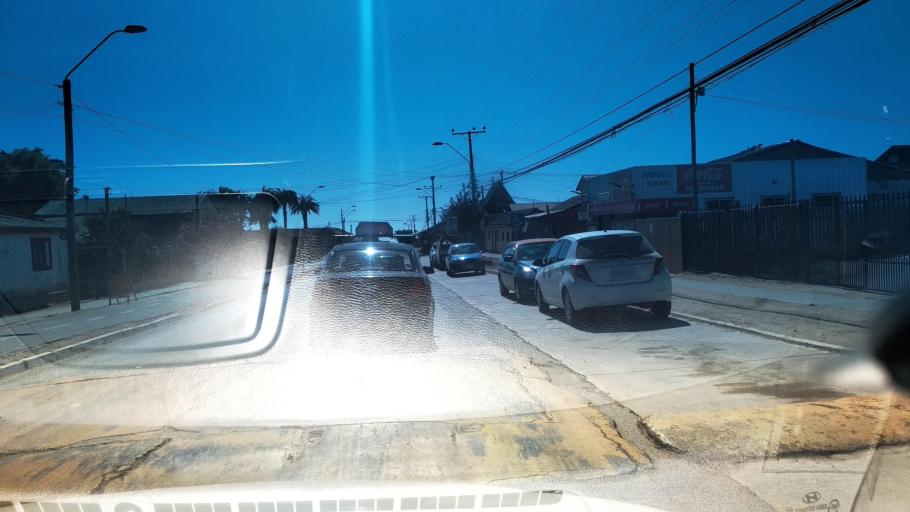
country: CL
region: O'Higgins
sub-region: Provincia de Colchagua
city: Santa Cruz
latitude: -34.3887
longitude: -71.9966
